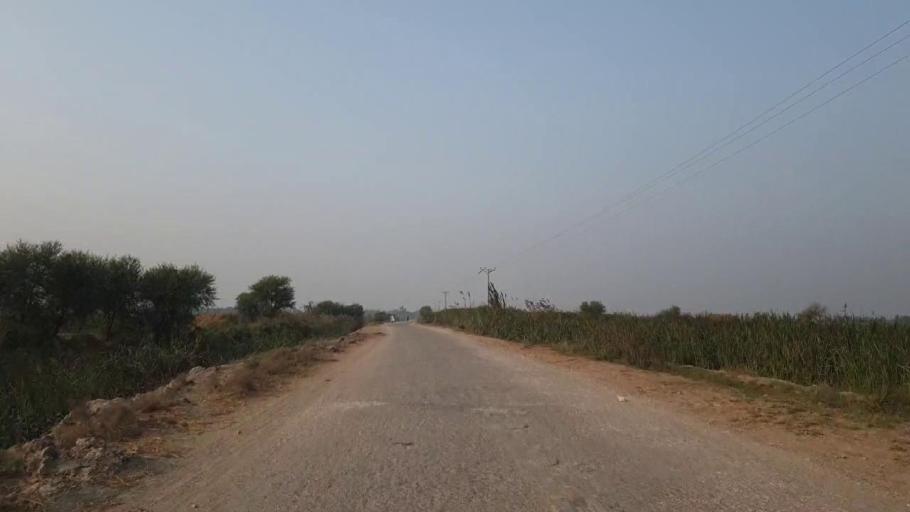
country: PK
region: Sindh
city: Tando Muhammad Khan
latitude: 25.1047
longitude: 68.4308
